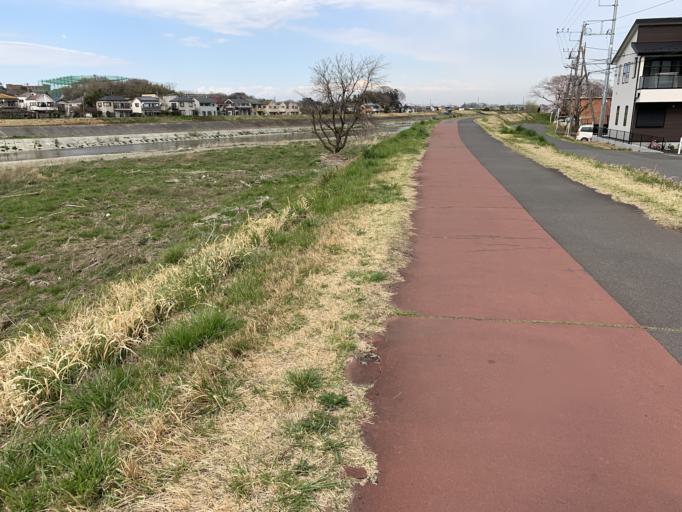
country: JP
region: Tokyo
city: Hino
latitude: 35.6607
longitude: 139.3943
